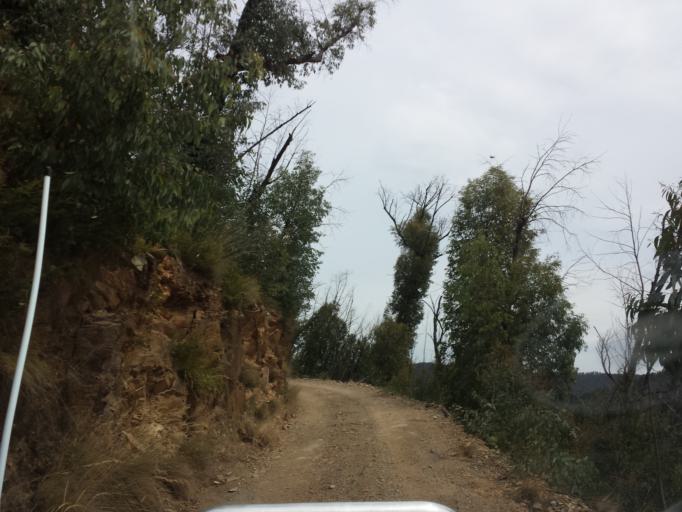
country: AU
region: Victoria
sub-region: Wellington
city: Heyfield
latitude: -37.7566
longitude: 146.5163
